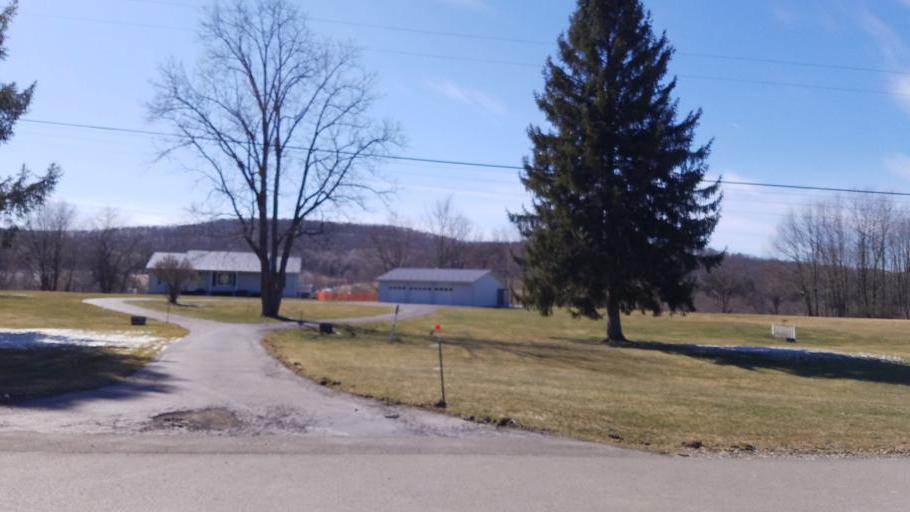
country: US
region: New York
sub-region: Allegany County
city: Wellsville
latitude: 42.0393
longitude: -77.9138
